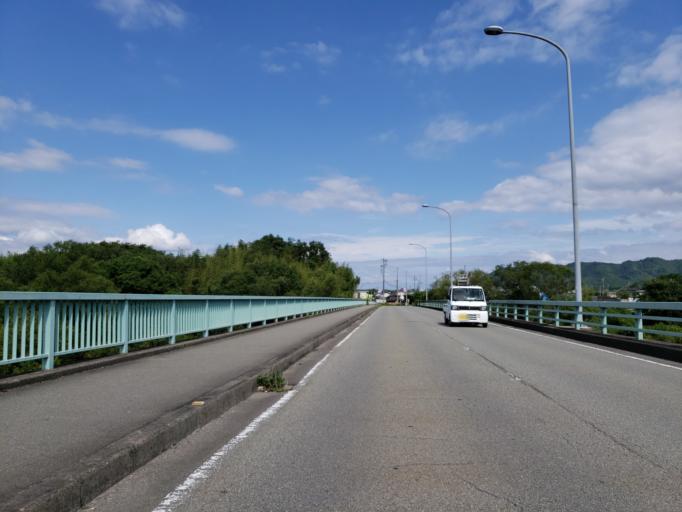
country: JP
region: Hyogo
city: Himeji
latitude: 34.9136
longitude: 134.7461
